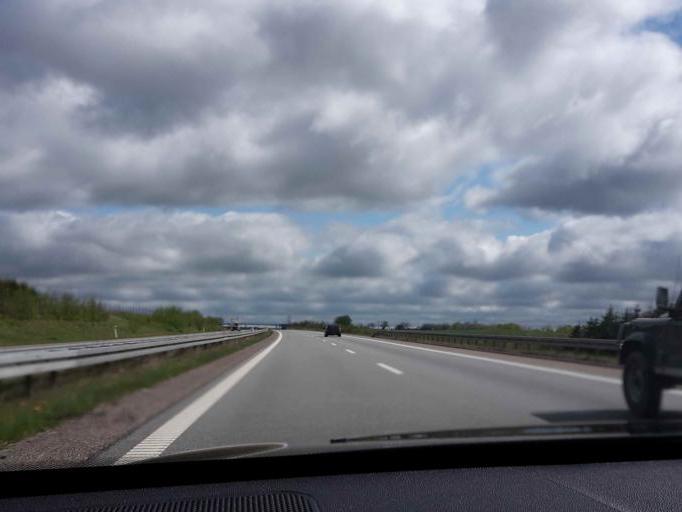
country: DK
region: Central Jutland
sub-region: Arhus Kommune
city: Hjortshoj
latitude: 56.2421
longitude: 10.2885
